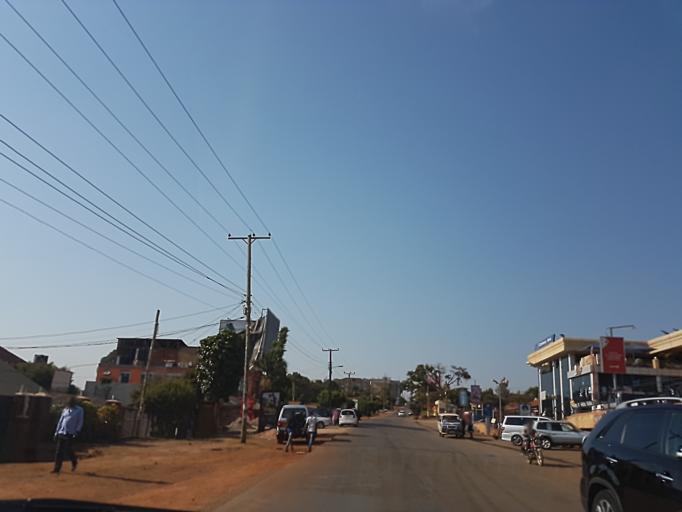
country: UG
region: Central Region
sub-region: Wakiso District
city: Kireka
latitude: 0.3489
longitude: 32.6164
